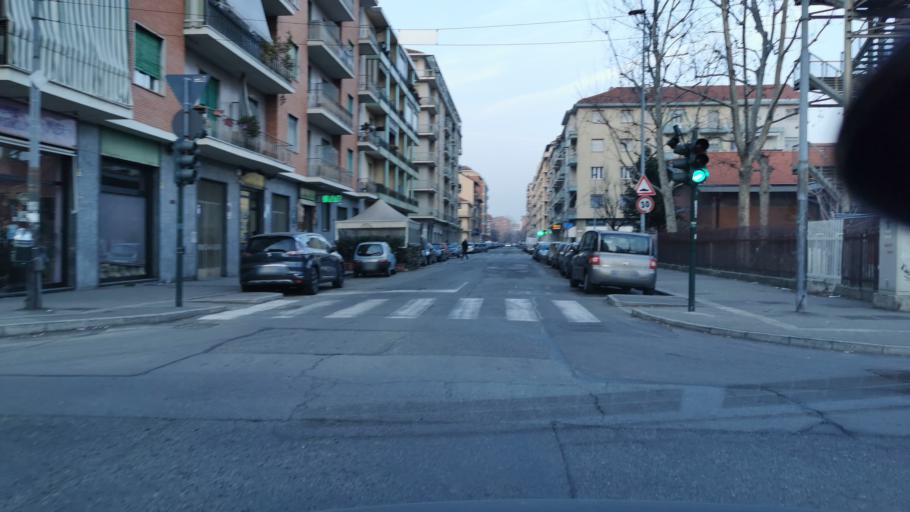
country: IT
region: Piedmont
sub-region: Provincia di Torino
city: Venaria Reale
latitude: 45.0981
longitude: 7.6535
